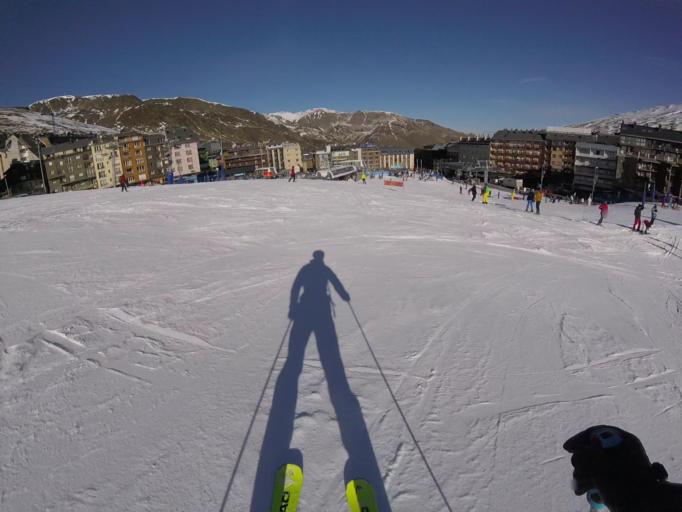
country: AD
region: Encamp
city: Pas de la Casa
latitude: 42.5398
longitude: 1.7327
